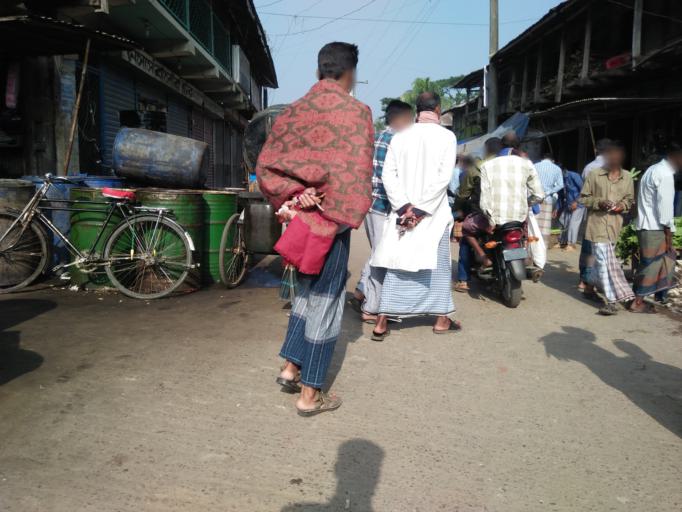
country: BD
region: Khulna
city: Uttar Char Fasson
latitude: 22.1917
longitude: 90.6741
